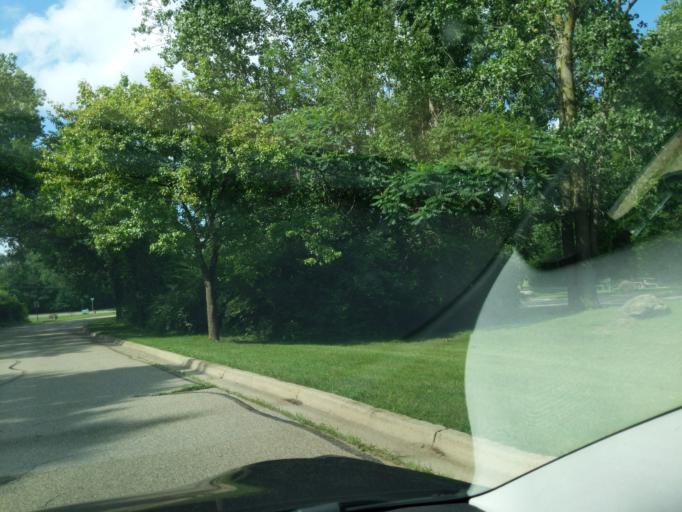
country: US
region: Michigan
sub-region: Jackson County
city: Jackson
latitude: 42.2317
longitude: -84.3728
